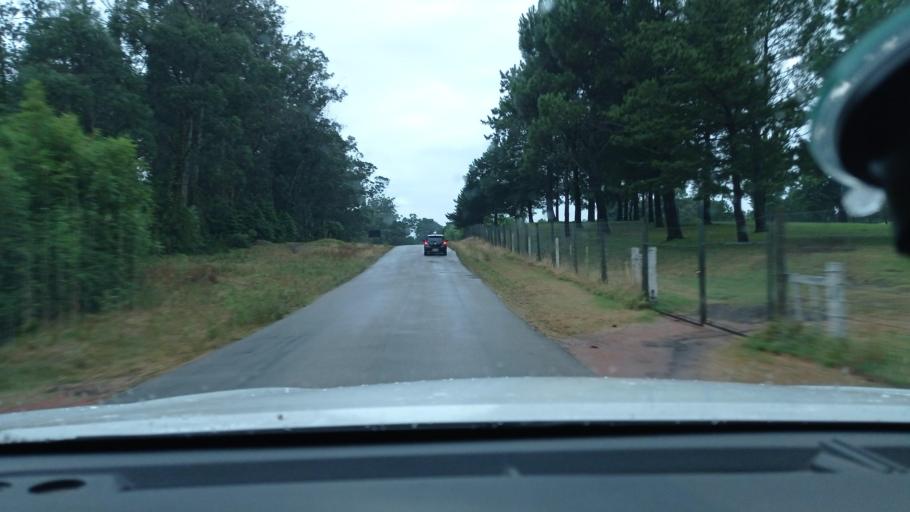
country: UY
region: Maldonado
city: Maldonado
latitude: -34.9244
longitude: -54.9086
